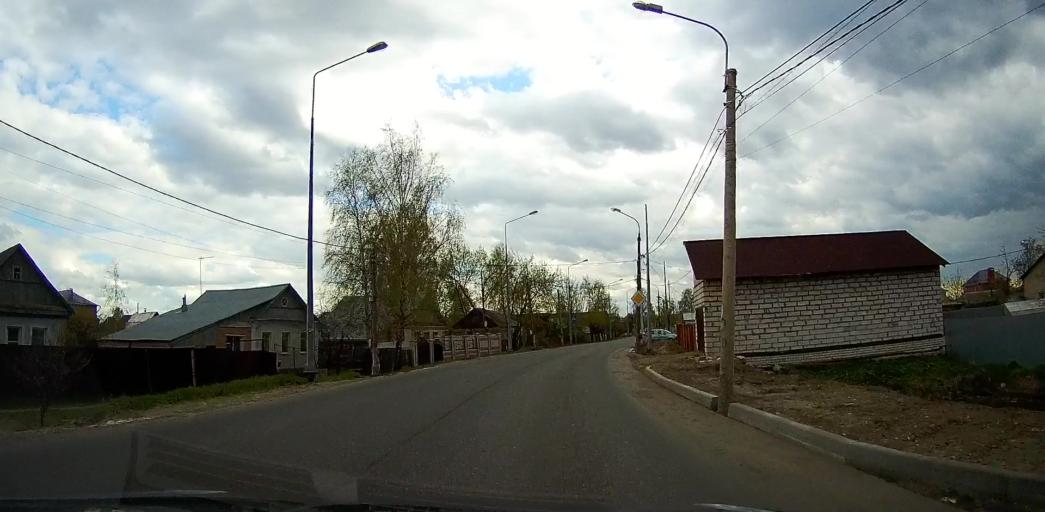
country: RU
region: Moskovskaya
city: Pavlovskiy Posad
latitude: 55.7960
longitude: 38.6890
